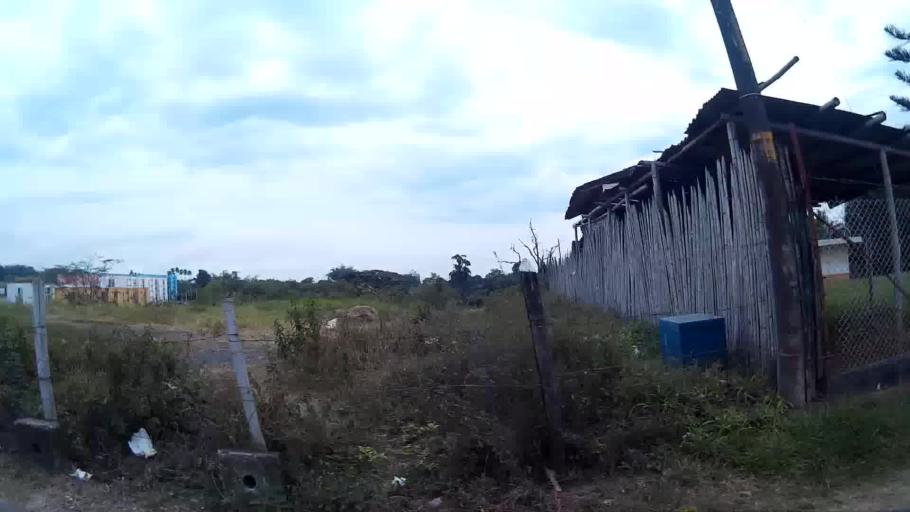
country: CO
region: Risaralda
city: Pereira
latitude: 4.7889
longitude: -75.7319
